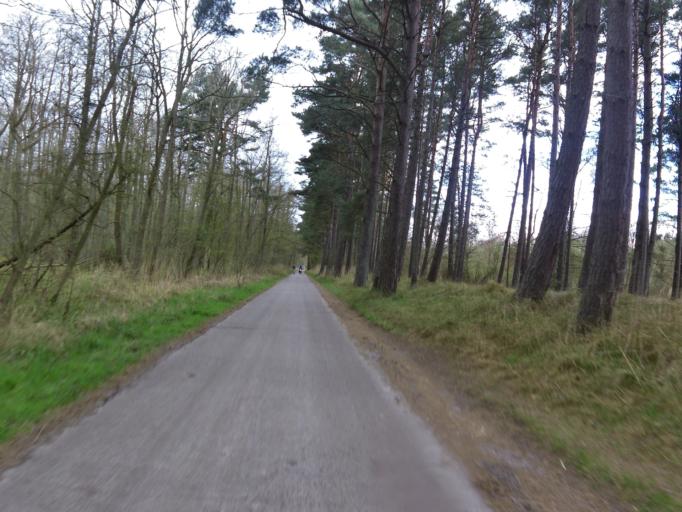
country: DE
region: Mecklenburg-Vorpommern
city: Ostseebad Prerow
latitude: 54.4640
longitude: 12.5268
